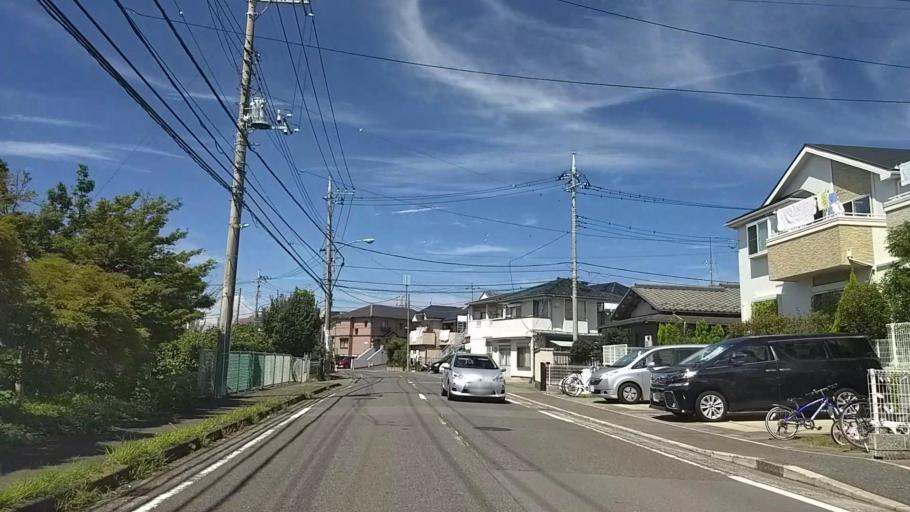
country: JP
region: Tokyo
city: Chofugaoka
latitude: 35.5586
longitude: 139.5666
